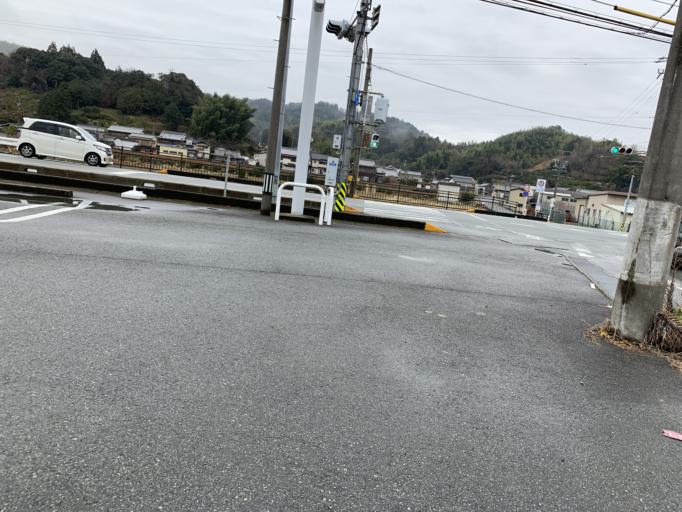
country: JP
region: Mie
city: Ise
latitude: 34.4783
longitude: 136.5419
